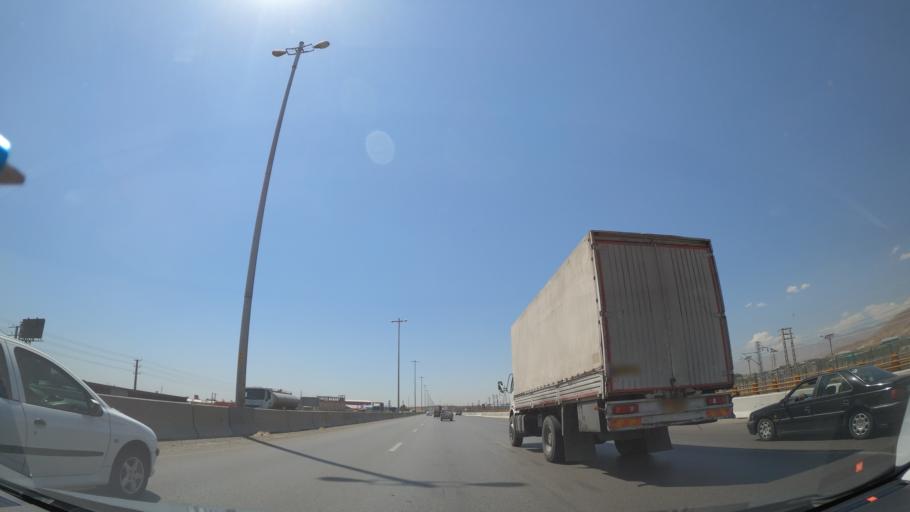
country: IR
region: Alborz
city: Karaj
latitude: 35.9055
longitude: 50.8464
